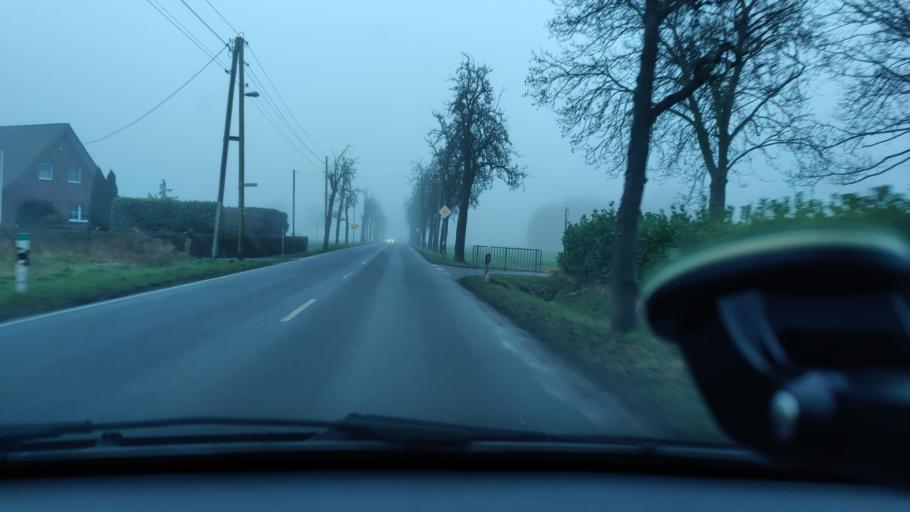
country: DE
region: North Rhine-Westphalia
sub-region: Regierungsbezirk Dusseldorf
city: Mehrhoog
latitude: 51.7322
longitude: 6.4611
